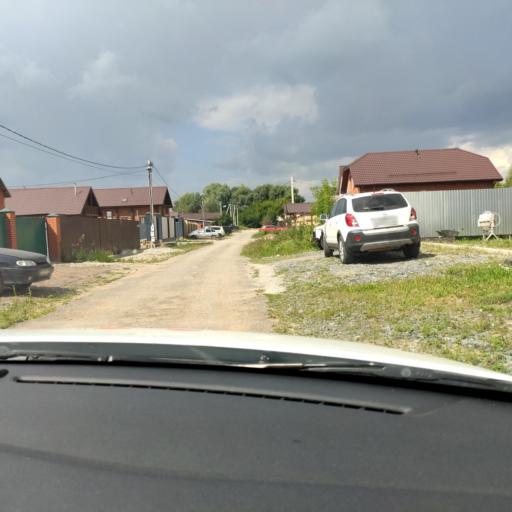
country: RU
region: Tatarstan
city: Stolbishchi
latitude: 55.7470
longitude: 49.2810
